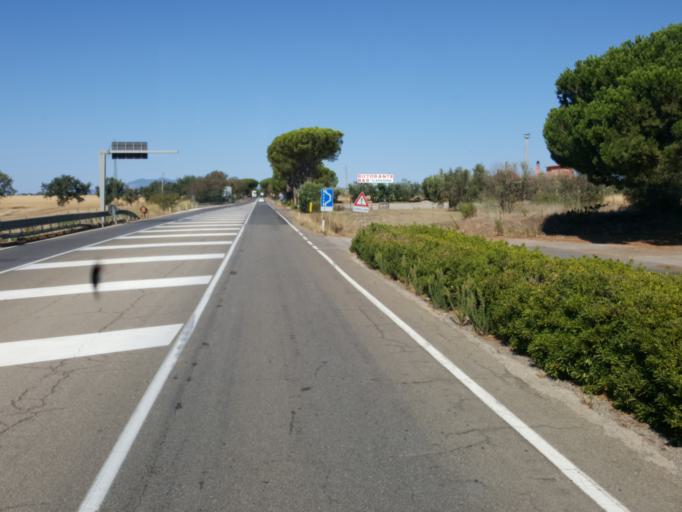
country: IT
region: Latium
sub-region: Provincia di Viterbo
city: Pescia Romana
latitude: 42.4143
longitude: 11.4618
